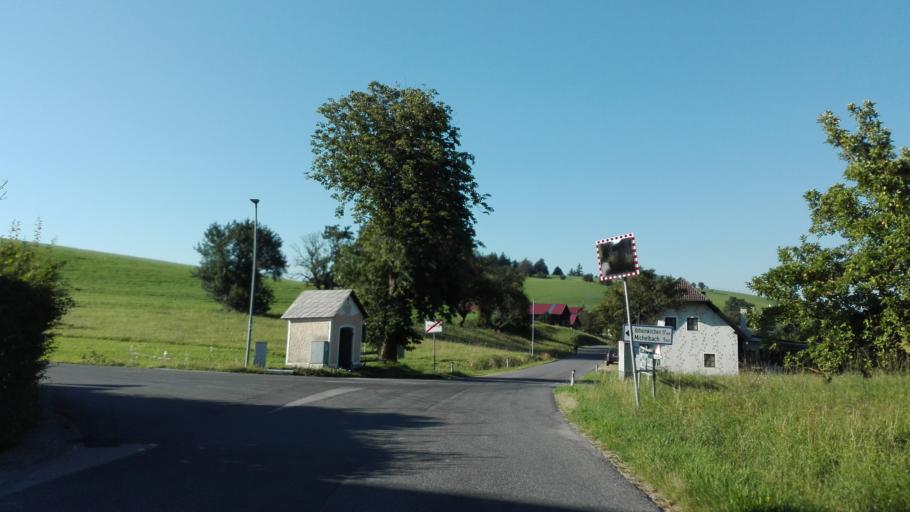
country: AT
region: Lower Austria
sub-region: Politischer Bezirk Sankt Polten
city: Stossing
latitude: 48.0904
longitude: 15.8245
